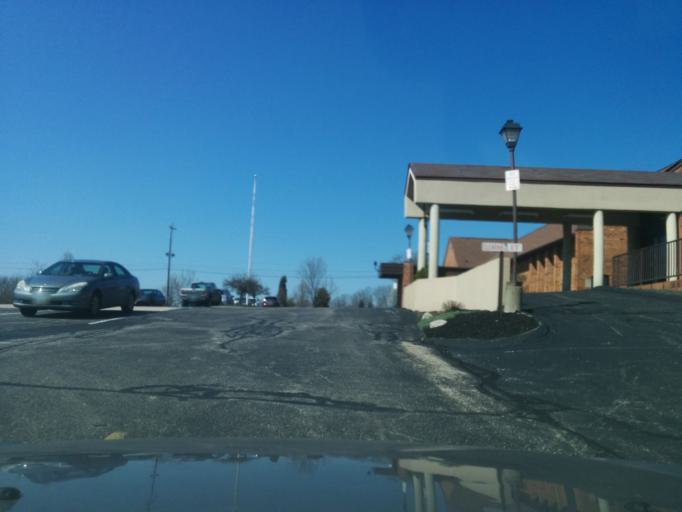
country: US
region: Ohio
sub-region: Hamilton County
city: Dry Ridge
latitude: 39.2454
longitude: -84.6113
